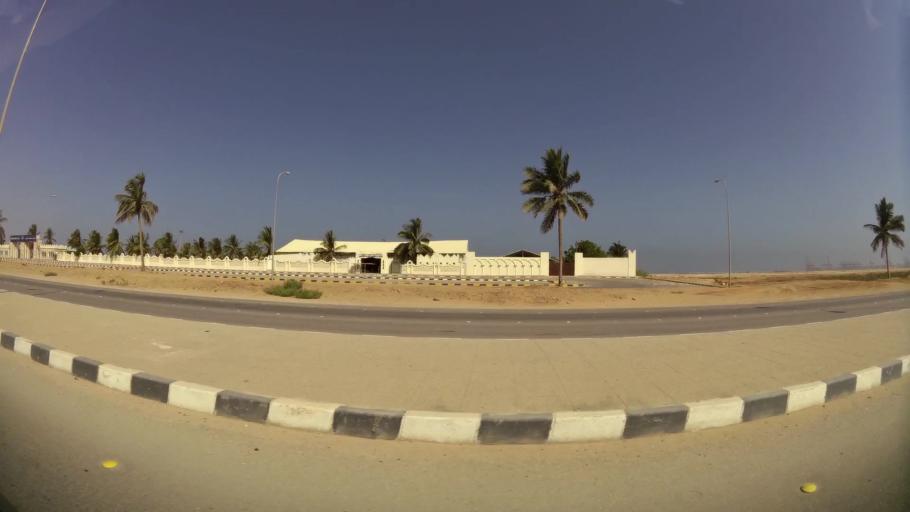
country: OM
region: Zufar
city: Salalah
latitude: 16.9893
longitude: 54.0237
